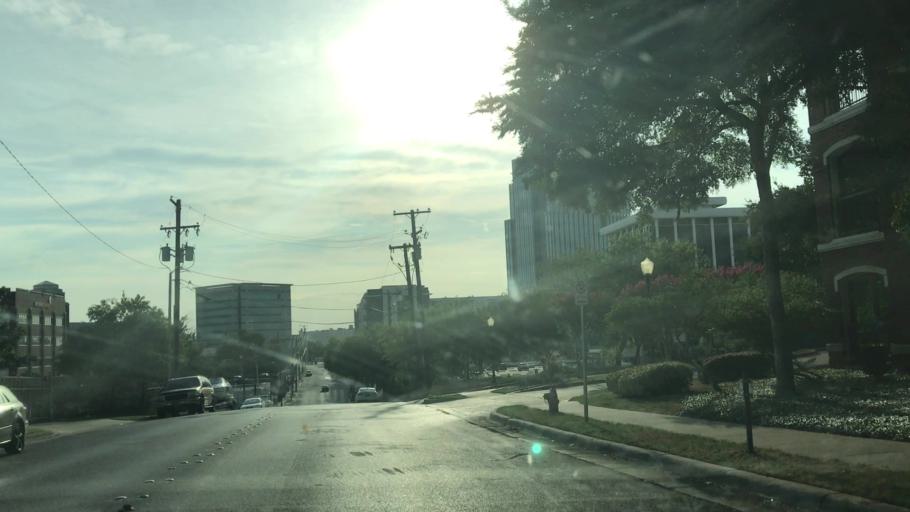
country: US
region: Texas
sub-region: Tarrant County
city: Fort Worth
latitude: 32.7518
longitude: -97.3389
